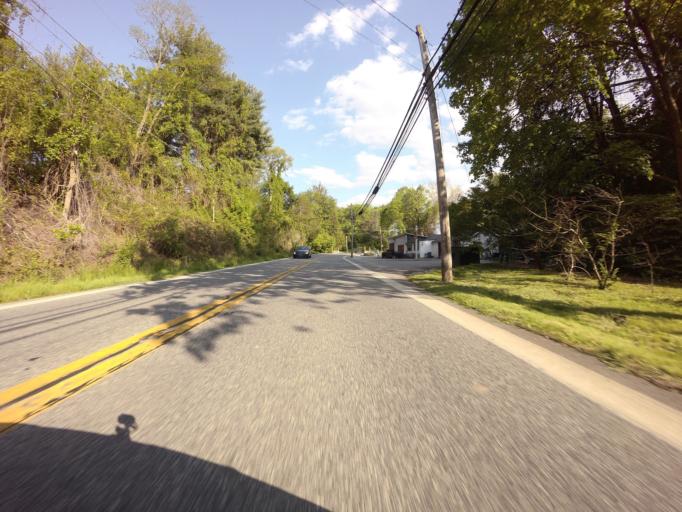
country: US
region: Maryland
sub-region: Baltimore County
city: Mays Chapel
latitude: 39.4586
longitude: -76.6968
